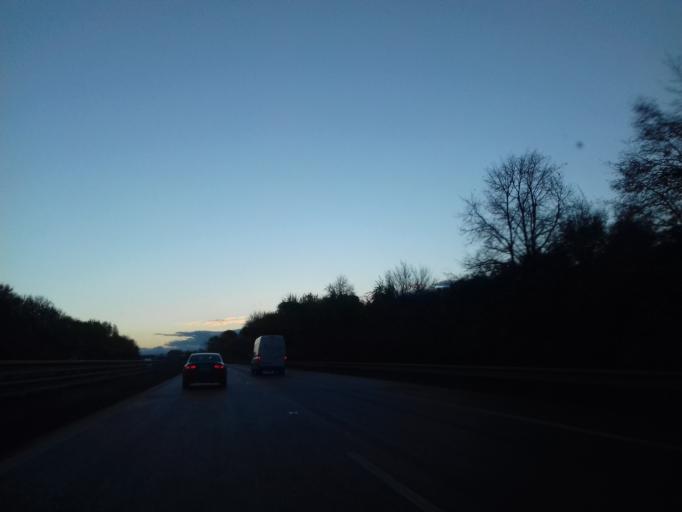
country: CZ
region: South Moravian
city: Tvarozna
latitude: 49.1812
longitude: 16.7770
